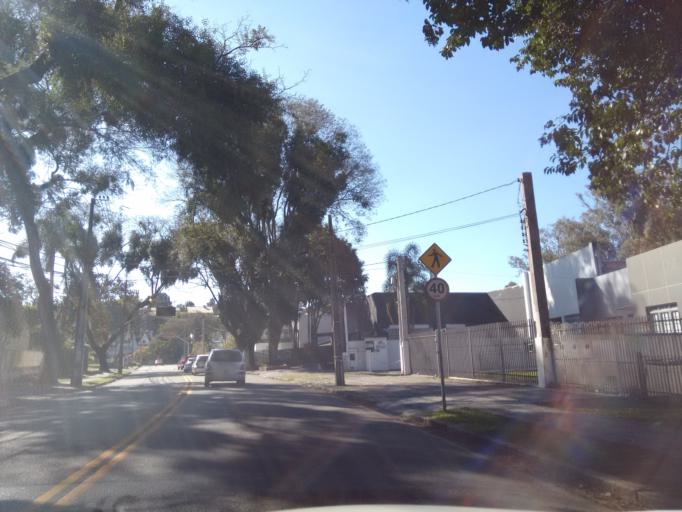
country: BR
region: Parana
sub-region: Curitiba
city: Curitiba
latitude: -25.3962
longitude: -49.2711
